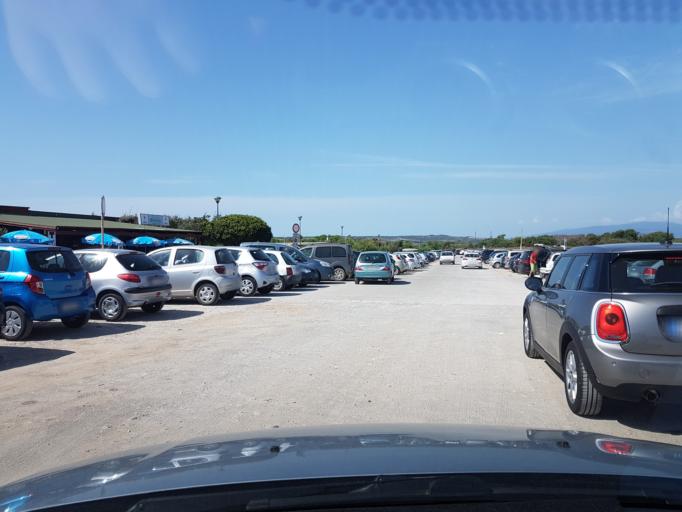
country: IT
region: Sardinia
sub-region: Provincia di Oristano
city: Cabras
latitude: 39.8786
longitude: 8.4392
